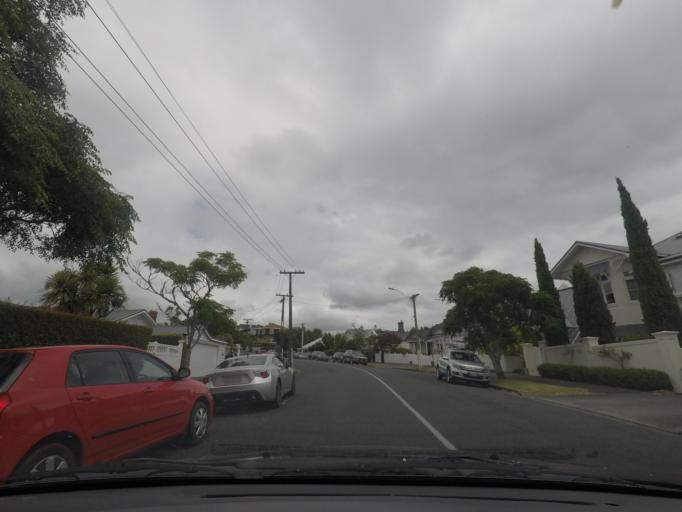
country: NZ
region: Auckland
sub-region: Auckland
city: Auckland
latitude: -36.8693
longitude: 174.7838
